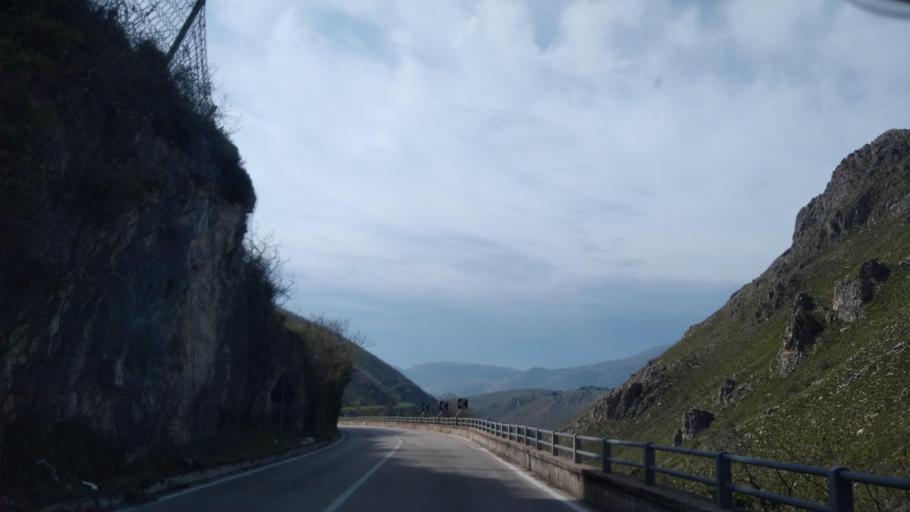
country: IT
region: Sicily
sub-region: Palermo
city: Montelepre
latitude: 38.0504
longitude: 13.1886
